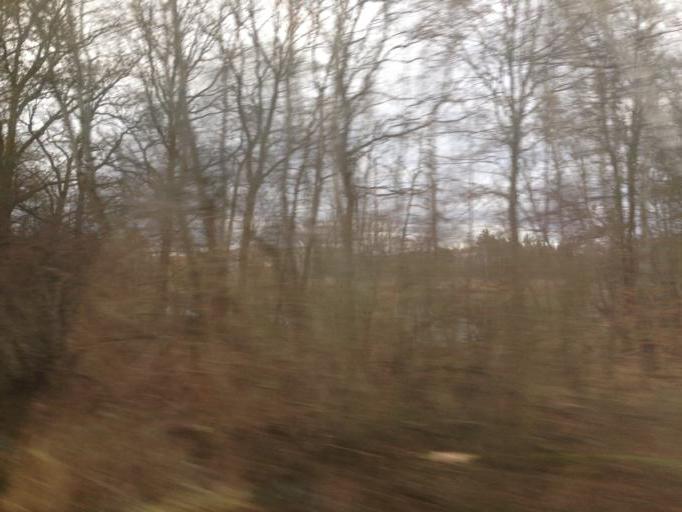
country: DE
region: Hesse
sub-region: Regierungsbezirk Giessen
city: Giessen
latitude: 50.5618
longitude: 8.6906
